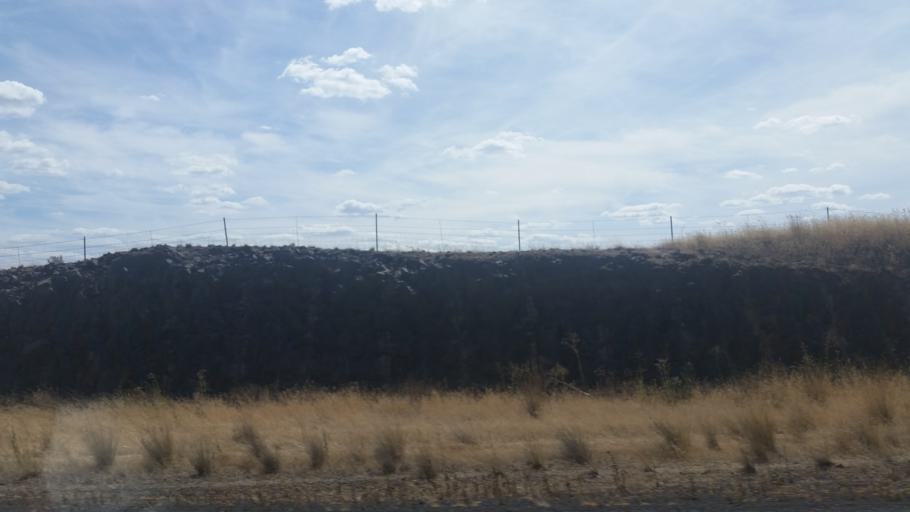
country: US
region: Washington
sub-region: Adams County
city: Ritzville
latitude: 47.2816
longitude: -118.0463
